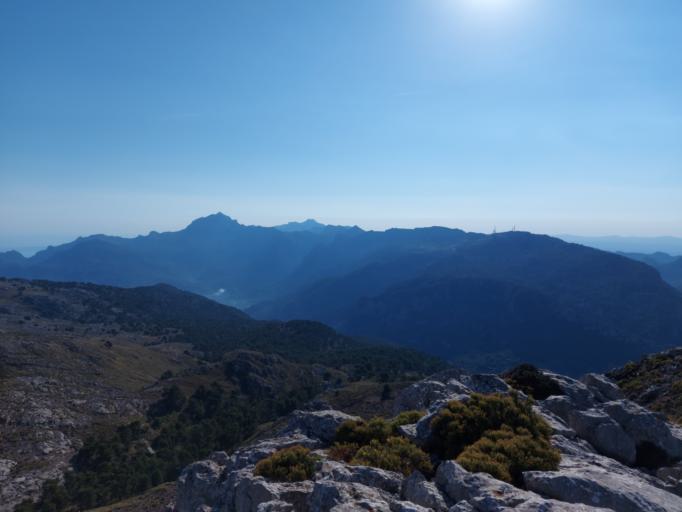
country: ES
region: Balearic Islands
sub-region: Illes Balears
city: Deia
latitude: 39.7327
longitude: 2.6640
